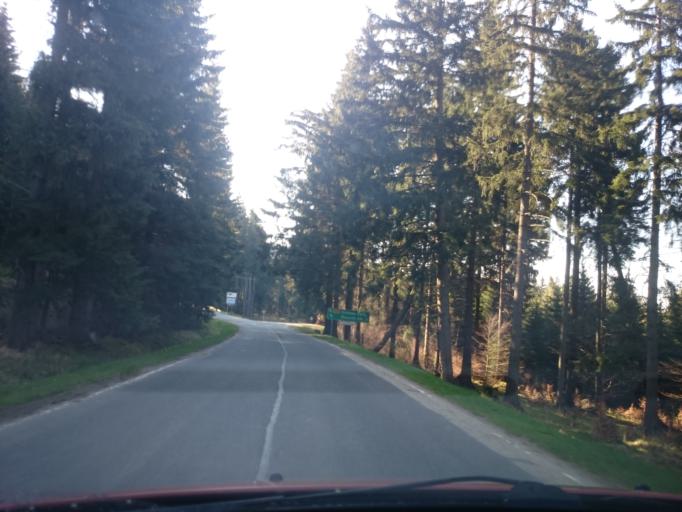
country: PL
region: Lower Silesian Voivodeship
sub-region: Powiat klodzki
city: Duszniki-Zdroj
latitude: 50.3298
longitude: 16.4075
